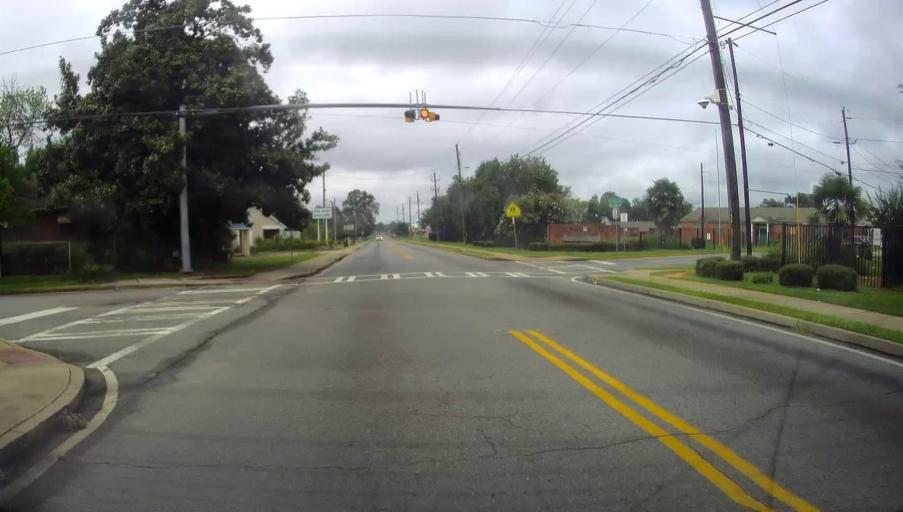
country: US
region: Georgia
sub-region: Bibb County
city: Macon
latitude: 32.8018
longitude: -83.6508
